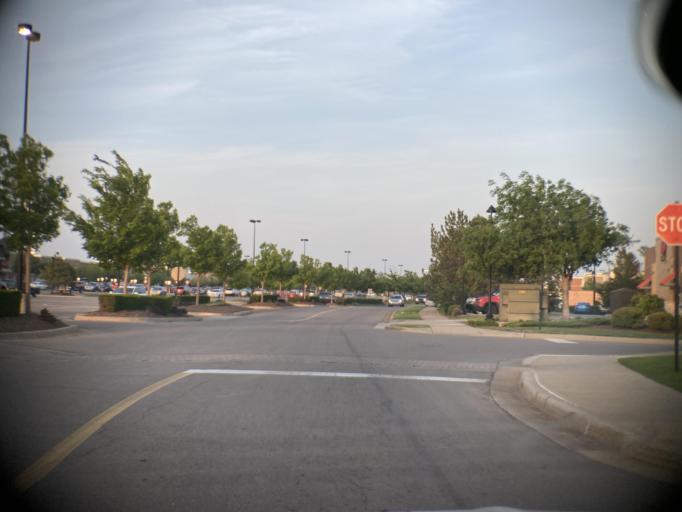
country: US
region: Oklahoma
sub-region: Oklahoma County
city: Midwest City
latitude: 35.4360
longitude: -97.3988
